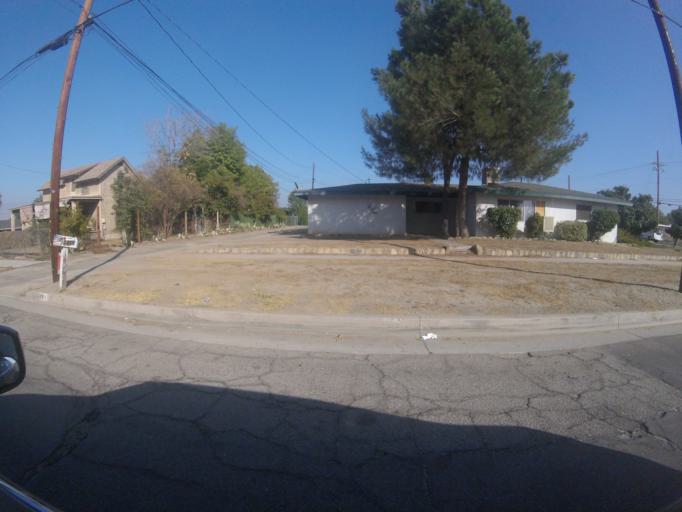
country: US
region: California
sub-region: San Bernardino County
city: Redlands
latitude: 34.0706
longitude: -117.1912
